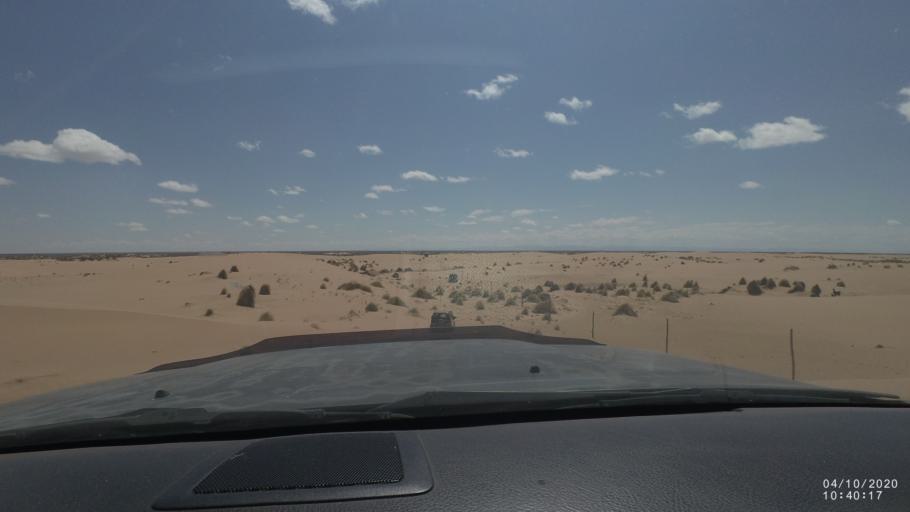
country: BO
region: Oruro
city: Poopo
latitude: -18.7057
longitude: -67.4729
